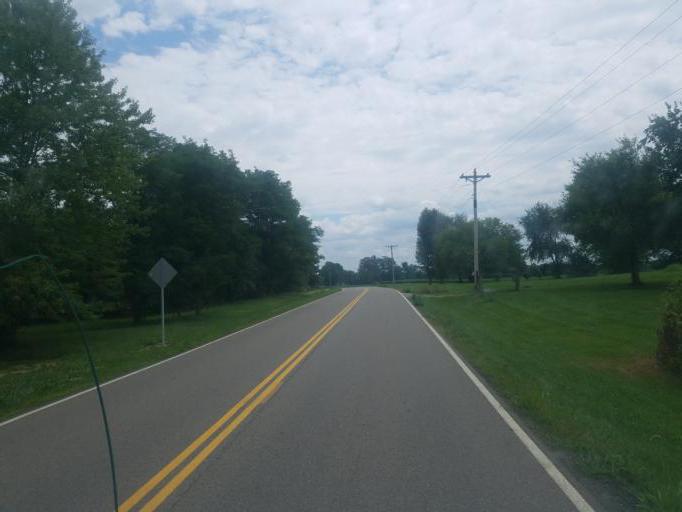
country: US
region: Ohio
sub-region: Licking County
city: Utica
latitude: 40.2040
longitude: -82.5341
